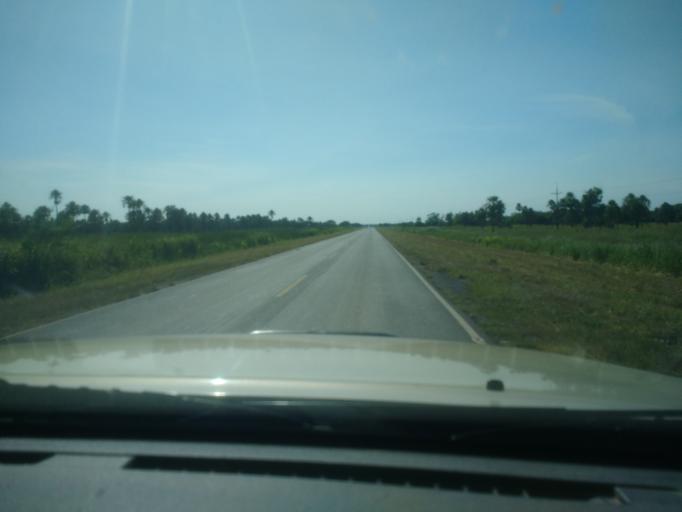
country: PY
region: Presidente Hayes
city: Benjamin Aceval
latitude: -24.9172
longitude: -57.6103
